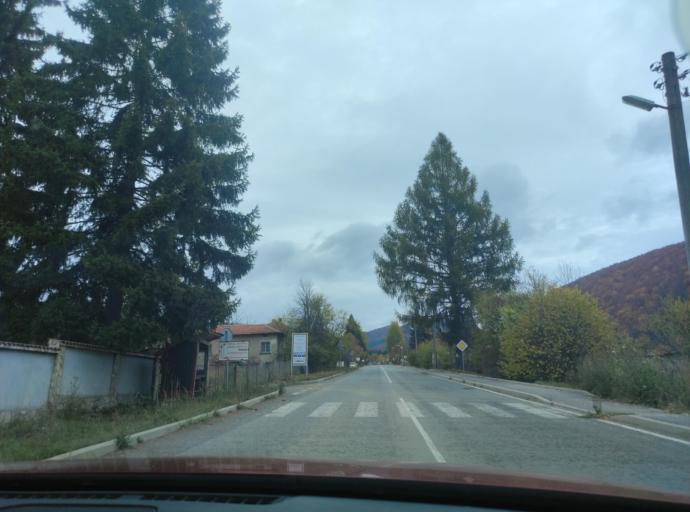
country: BG
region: Sofiya
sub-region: Obshtina Godech
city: Godech
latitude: 43.0936
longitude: 23.0989
